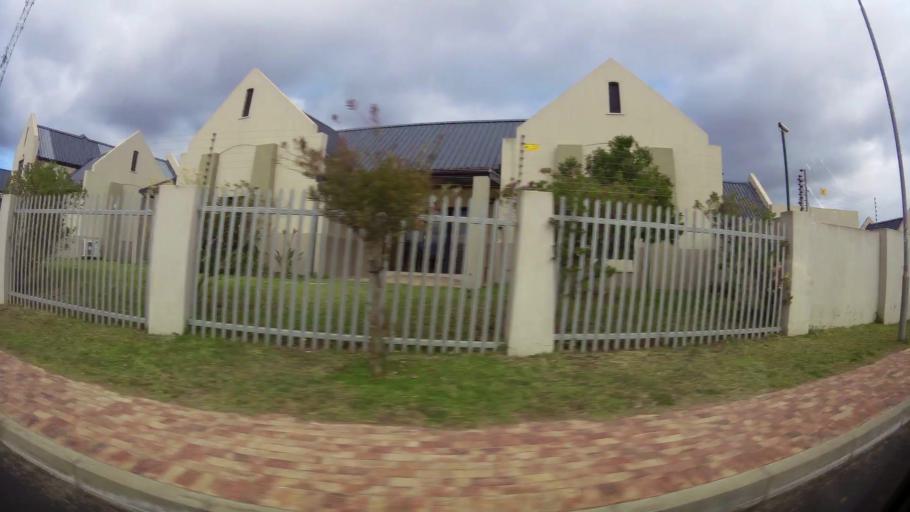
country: ZA
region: Western Cape
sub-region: Eden District Municipality
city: George
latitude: -33.9811
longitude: 22.4944
